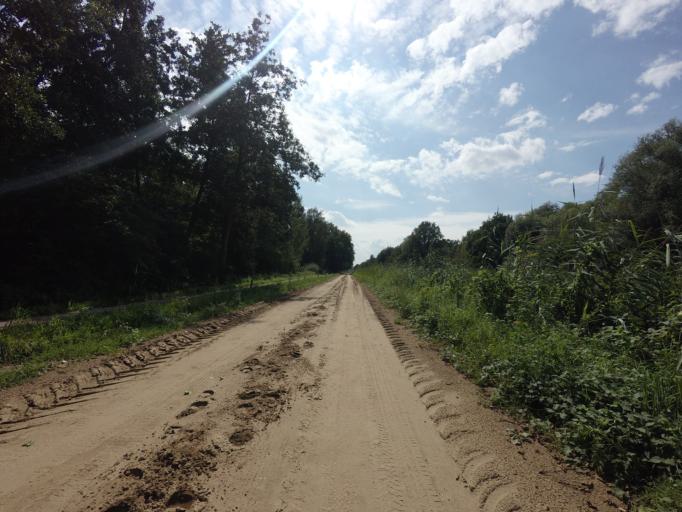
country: NL
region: Overijssel
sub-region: Gemeente Deventer
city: Schalkhaar
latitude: 52.2822
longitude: 6.2268
